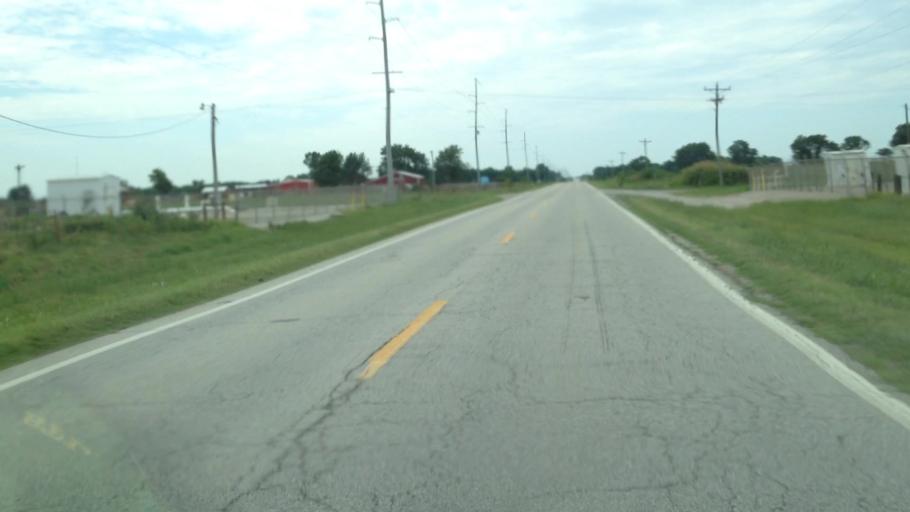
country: US
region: Kansas
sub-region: Labette County
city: Chetopa
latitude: 36.9020
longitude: -95.0896
